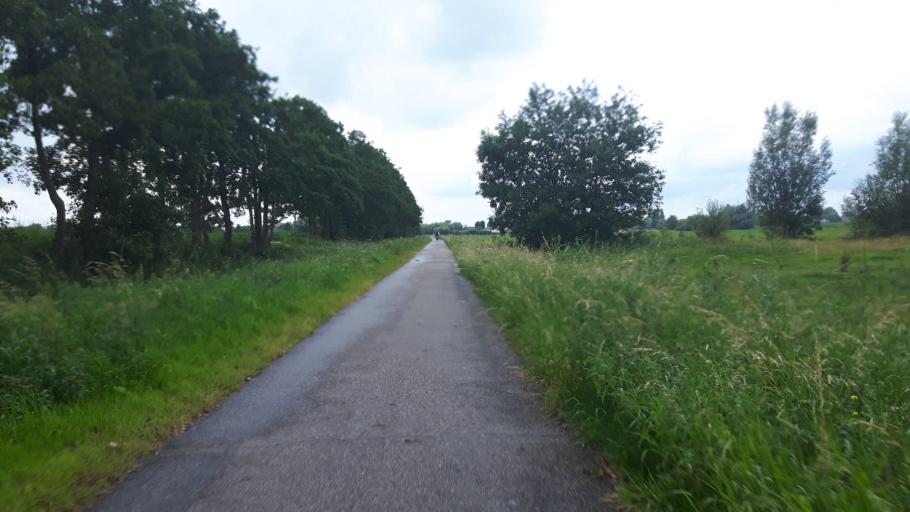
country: NL
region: South Holland
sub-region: Gemeente Vlist
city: Vlist
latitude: 51.9733
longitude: 4.8347
